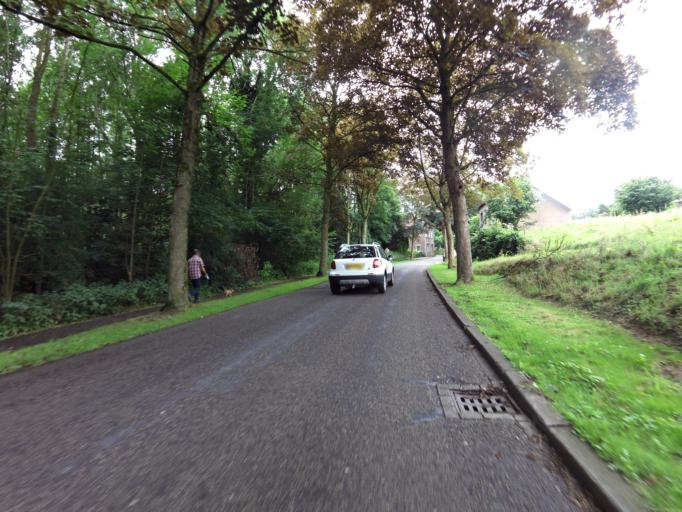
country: NL
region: Limburg
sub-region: Gemeente Nuth
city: Nuth
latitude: 50.9179
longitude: 5.8739
